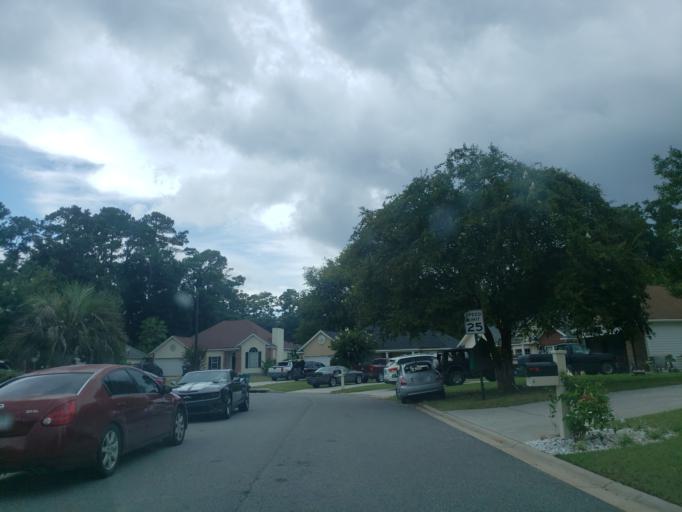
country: US
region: Georgia
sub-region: Chatham County
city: Wilmington Island
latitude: 32.0246
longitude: -80.9594
